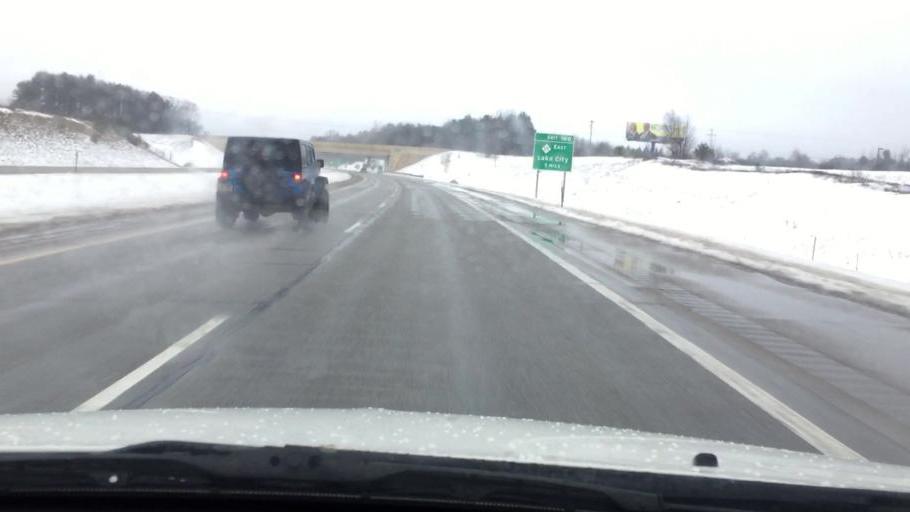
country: US
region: Michigan
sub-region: Wexford County
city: Cadillac
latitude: 44.2693
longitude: -85.3885
